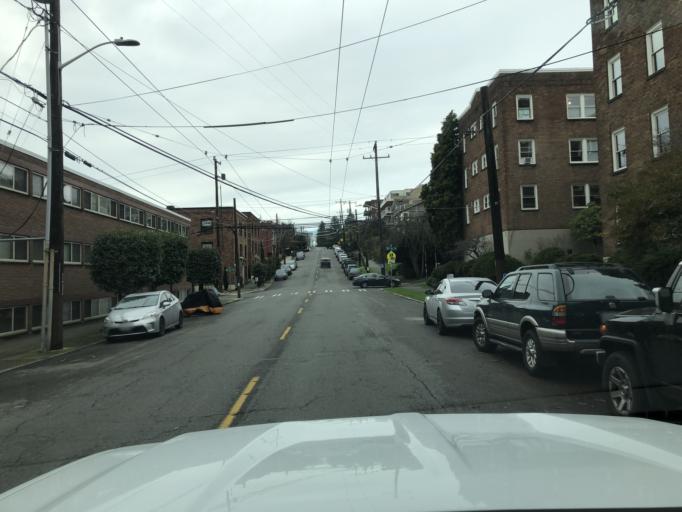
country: US
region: Washington
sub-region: King County
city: Seattle
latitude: 47.6267
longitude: -122.3599
